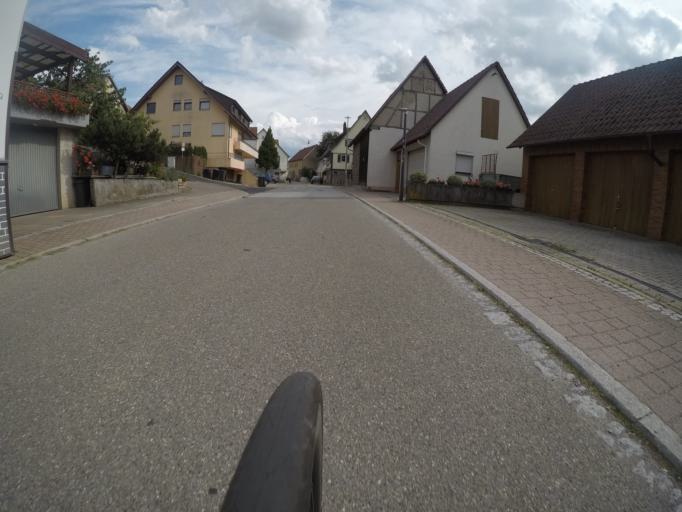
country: DE
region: Baden-Wuerttemberg
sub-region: Regierungsbezirk Stuttgart
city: Weil der Stadt
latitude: 48.7253
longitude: 8.8921
